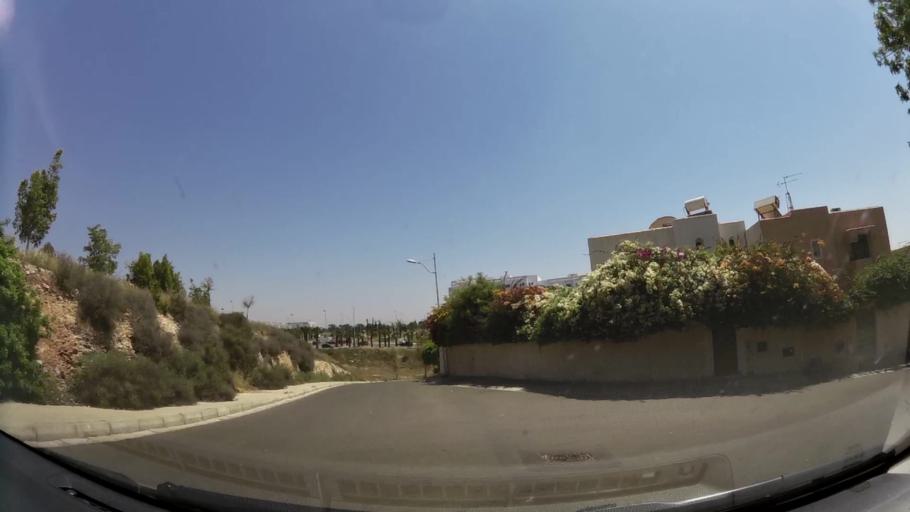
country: MA
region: Souss-Massa-Draa
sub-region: Agadir-Ida-ou-Tnan
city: Agadir
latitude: 30.4357
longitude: -9.5813
